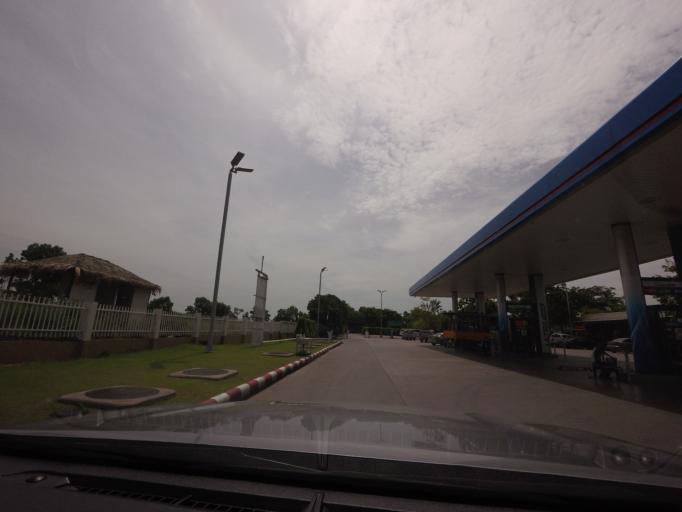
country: TH
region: Nakhon Si Thammarat
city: Nakhon Si Thammarat
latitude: 8.4396
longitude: 99.9833
